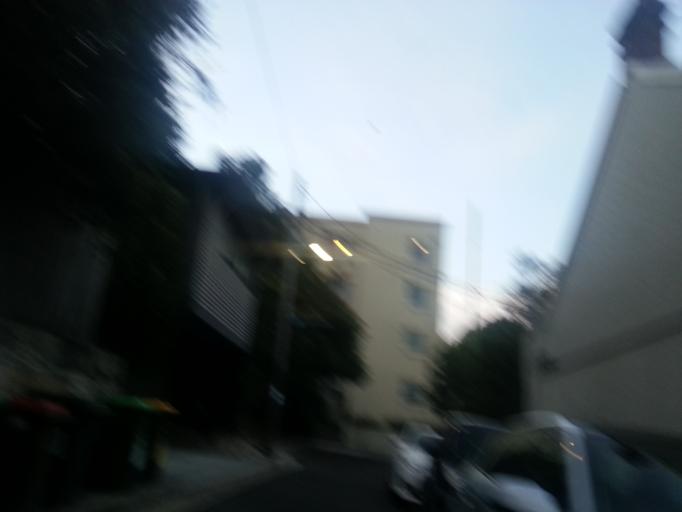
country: AU
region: New South Wales
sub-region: City of Sydney
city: Chippendale
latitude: -33.8775
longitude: 151.1870
